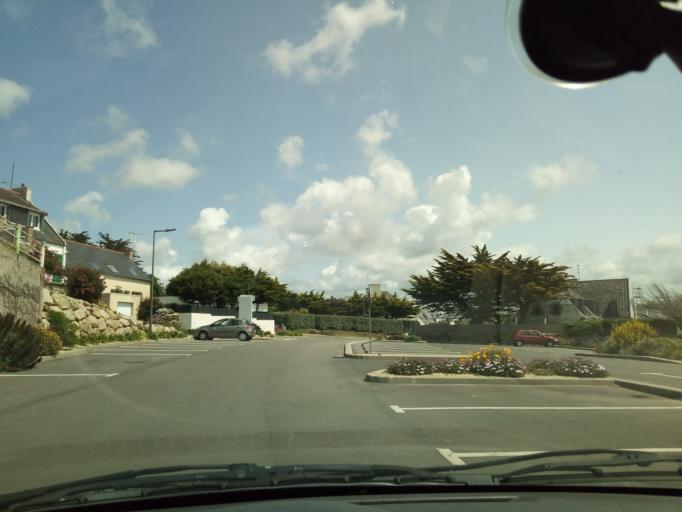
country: FR
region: Brittany
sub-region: Departement du Finistere
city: Audierne
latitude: 48.0113
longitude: -4.5522
